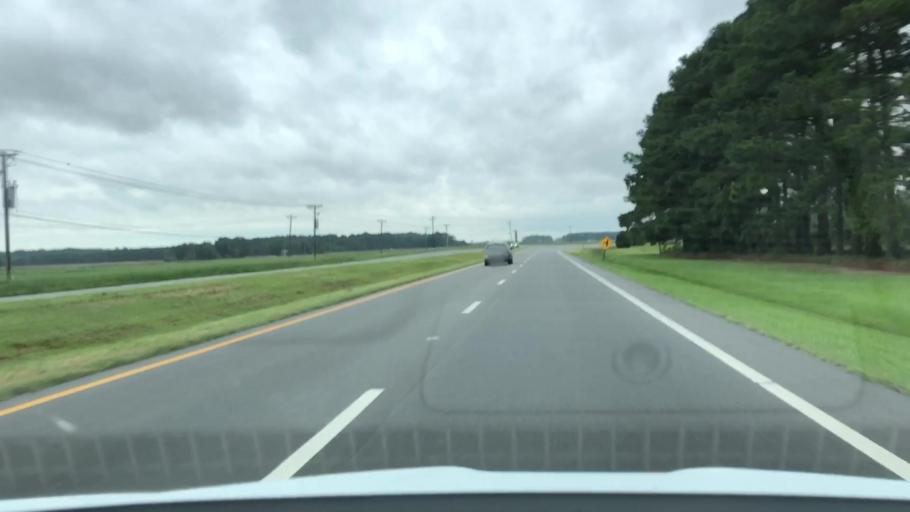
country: US
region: North Carolina
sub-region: Lenoir County
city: La Grange
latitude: 35.2602
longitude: -77.7100
